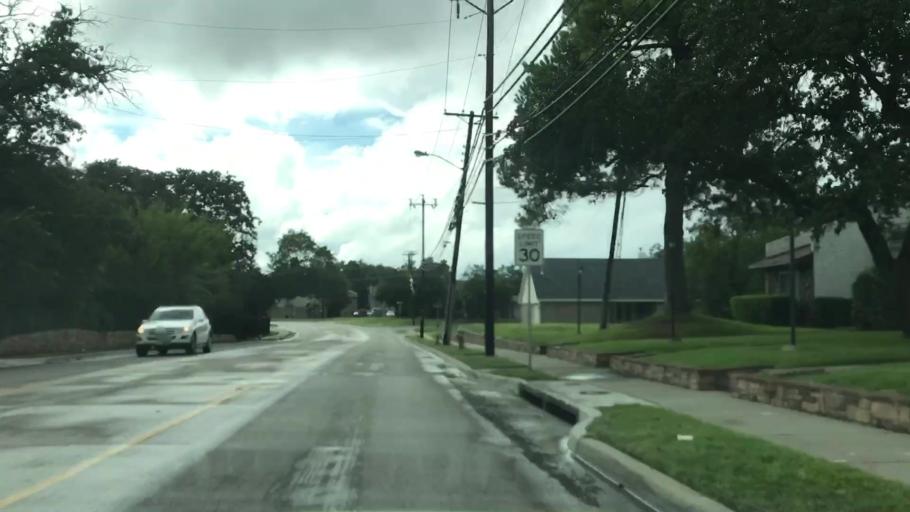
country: US
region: Texas
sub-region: Dallas County
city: Irving
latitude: 32.8308
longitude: -96.9233
